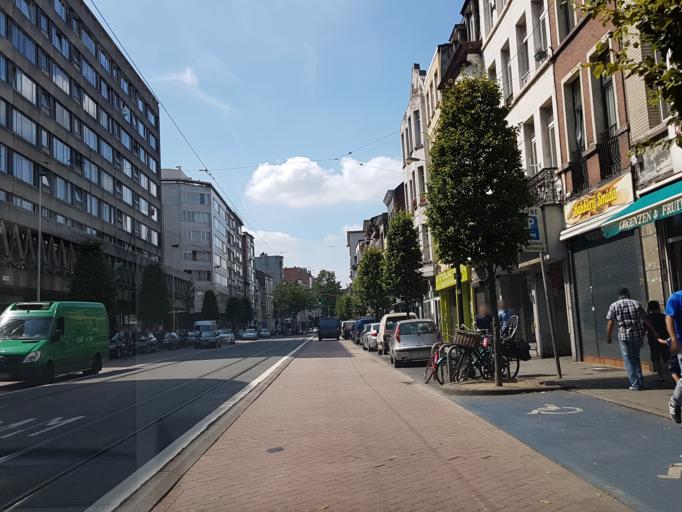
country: BE
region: Flanders
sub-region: Provincie Antwerpen
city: Antwerpen
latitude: 51.2144
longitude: 4.4371
